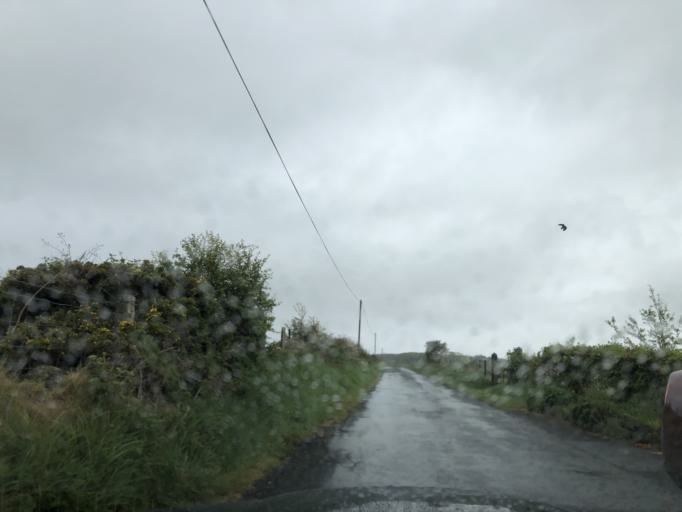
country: GB
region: Northern Ireland
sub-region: Moyle District
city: Ballycastle
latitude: 55.2069
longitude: -6.1661
